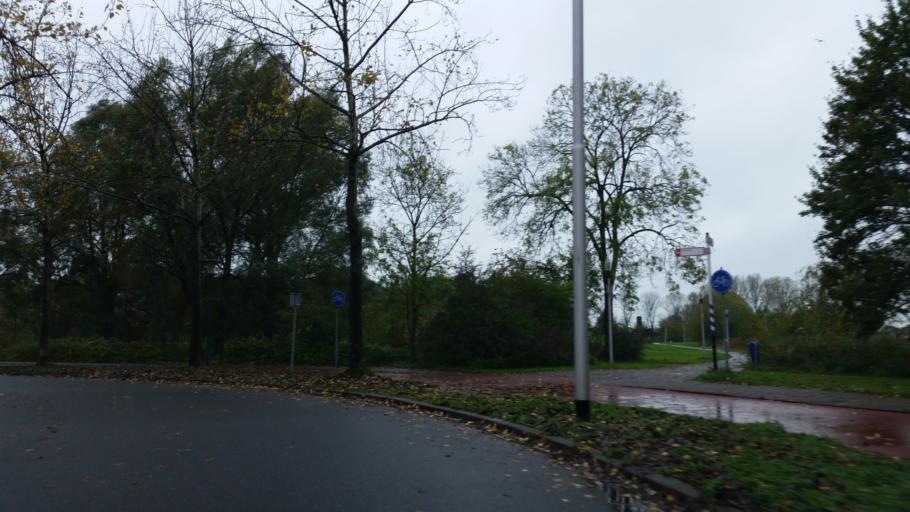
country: NL
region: Friesland
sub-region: Gemeente Leeuwarden
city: Bilgaard
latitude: 53.2110
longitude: 5.7958
